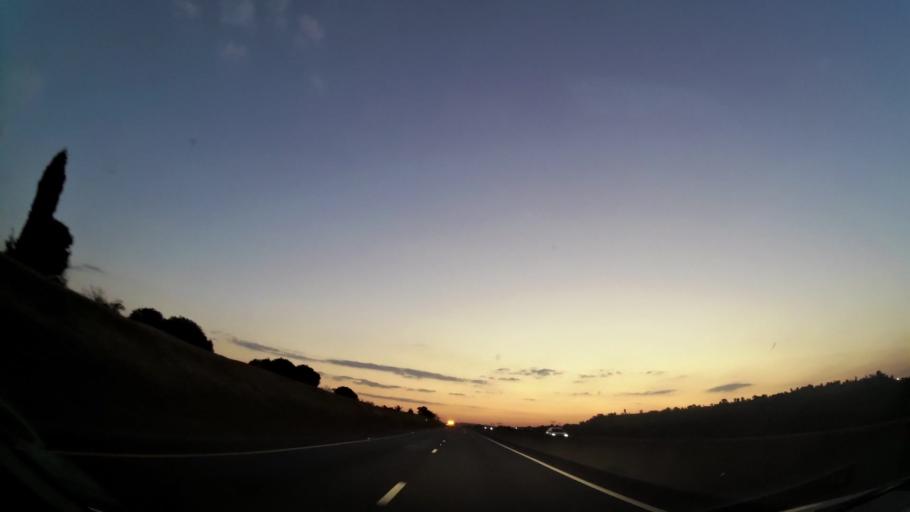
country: ZA
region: Gauteng
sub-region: Ekurhuleni Metropolitan Municipality
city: Germiston
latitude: -26.2378
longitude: 28.1070
